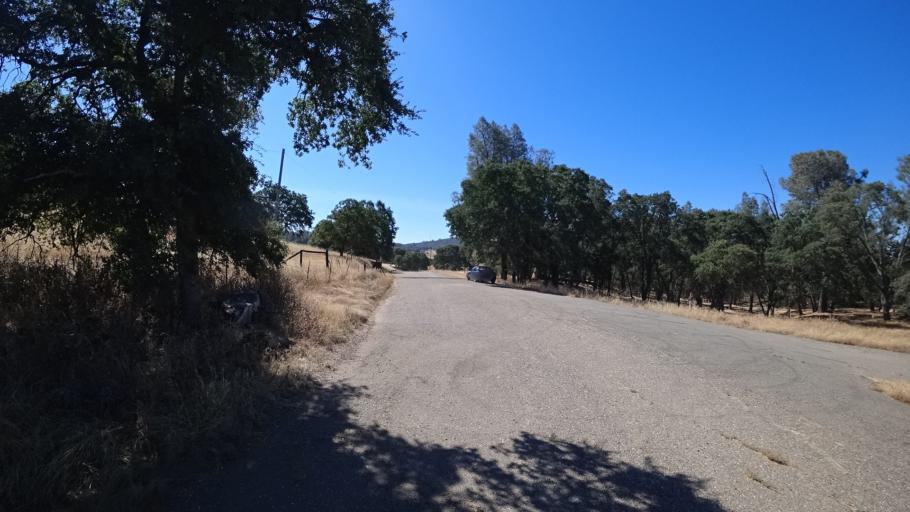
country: US
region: California
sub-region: Calaveras County
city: Valley Springs
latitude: 38.2335
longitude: -120.8584
